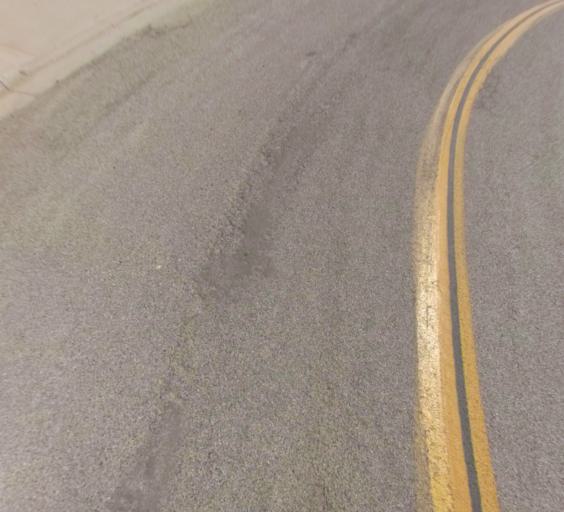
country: US
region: California
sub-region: Madera County
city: Bonadelle Ranchos-Madera Ranchos
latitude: 36.9013
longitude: -119.7968
